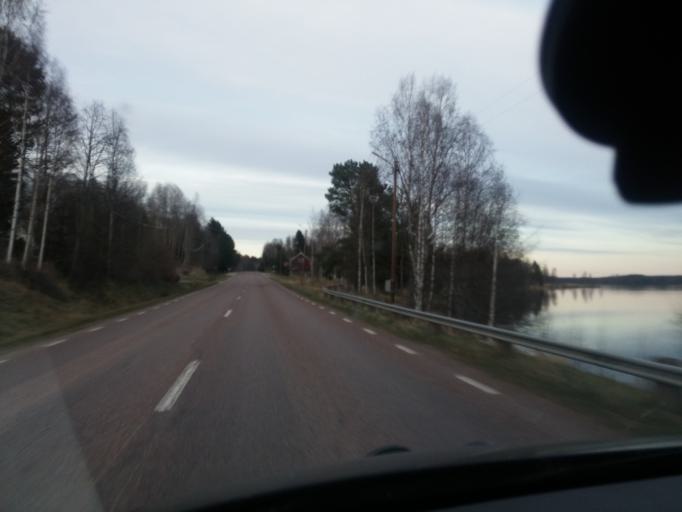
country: SE
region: Dalarna
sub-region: Faluns Kommun
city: Bjursas
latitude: 60.7146
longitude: 15.3220
